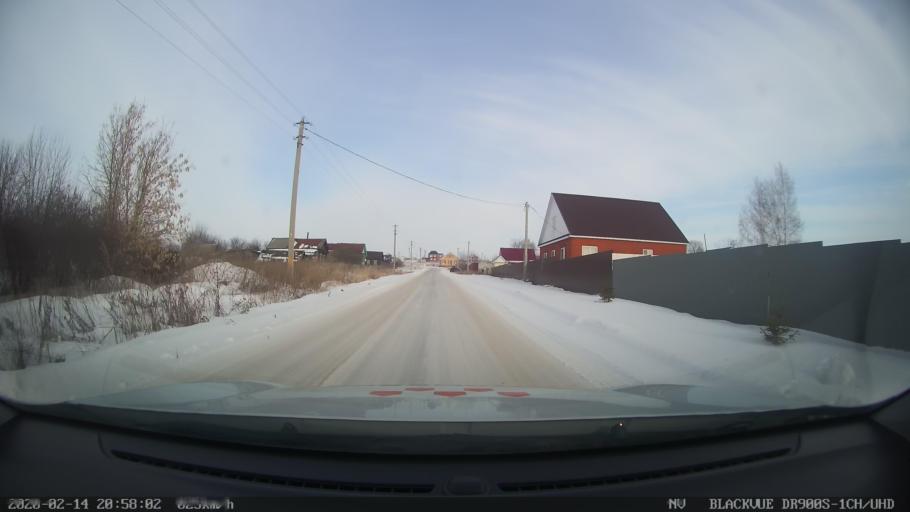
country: RU
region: Tatarstan
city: Kuybyshevskiy Zaton
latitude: 55.1771
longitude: 49.2476
